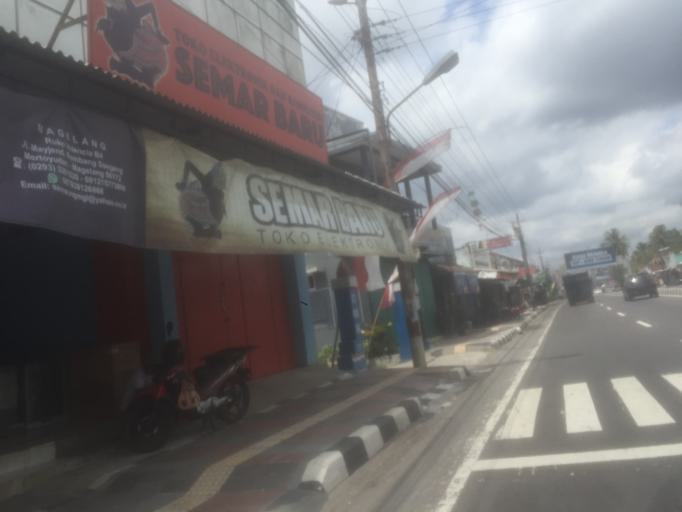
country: ID
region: Central Java
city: Muntilan
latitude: -7.6376
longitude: 110.3211
